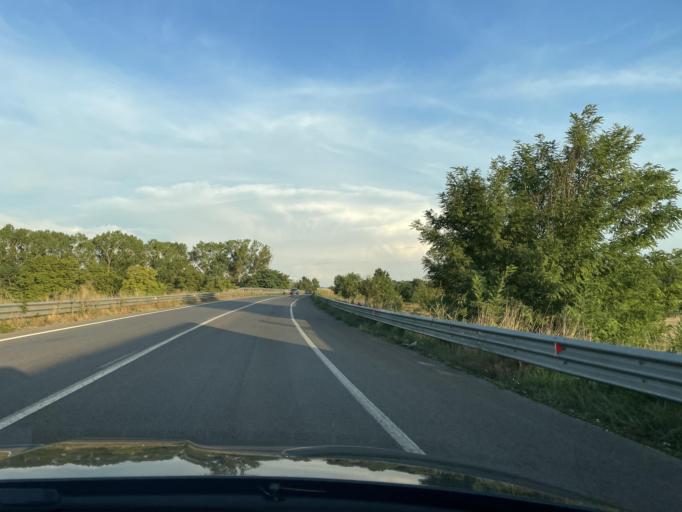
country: IT
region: Tuscany
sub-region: Provincia di Siena
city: Poggibonsi
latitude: 43.4855
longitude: 11.1177
